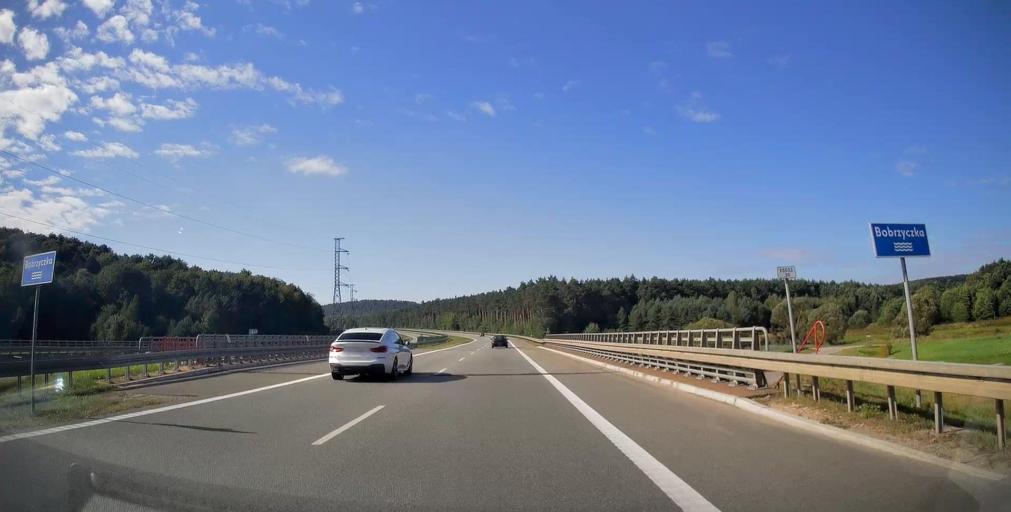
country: PL
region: Swietokrzyskie
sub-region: Powiat kielecki
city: Checiny
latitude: 50.8337
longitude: 20.4717
